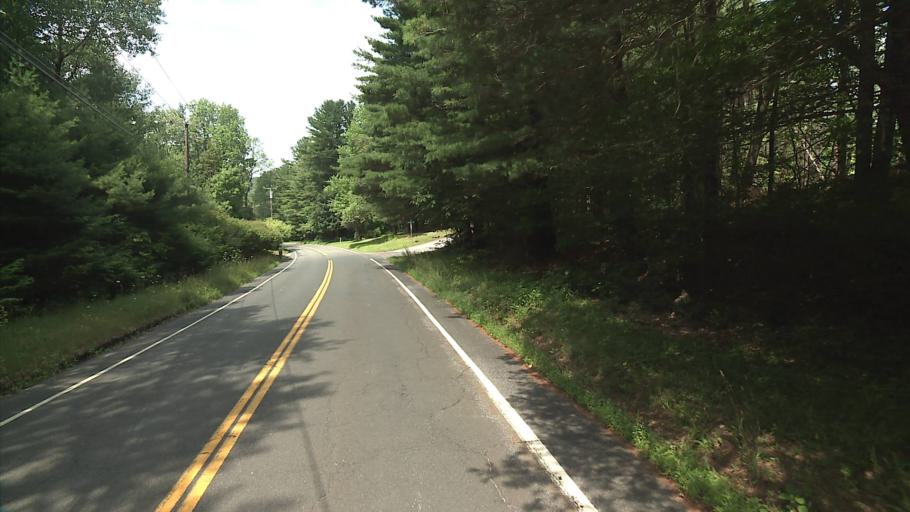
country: US
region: Connecticut
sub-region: Litchfield County
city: Winsted
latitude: 41.9840
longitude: -73.1123
